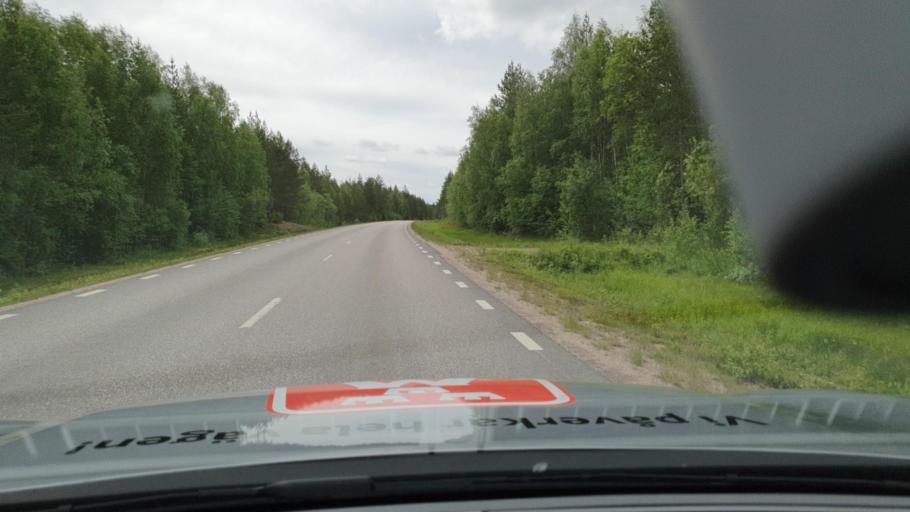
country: SE
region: Norrbotten
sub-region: Kalix Kommun
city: Kalix
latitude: 65.8567
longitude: 23.4764
